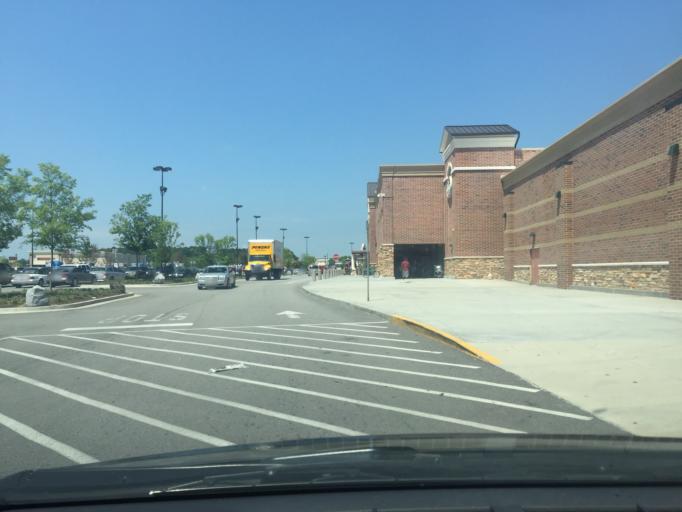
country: US
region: Georgia
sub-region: Chatham County
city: Isle of Hope
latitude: 32.0056
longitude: -81.1119
